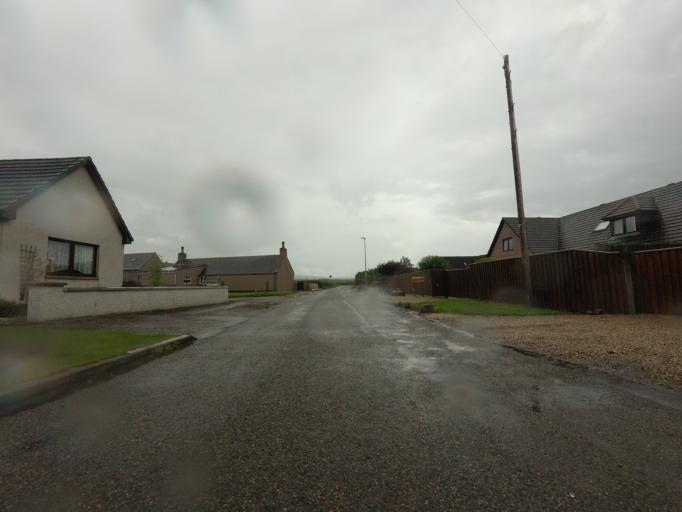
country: GB
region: Scotland
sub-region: Moray
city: Fochabers
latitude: 57.6601
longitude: -3.0733
